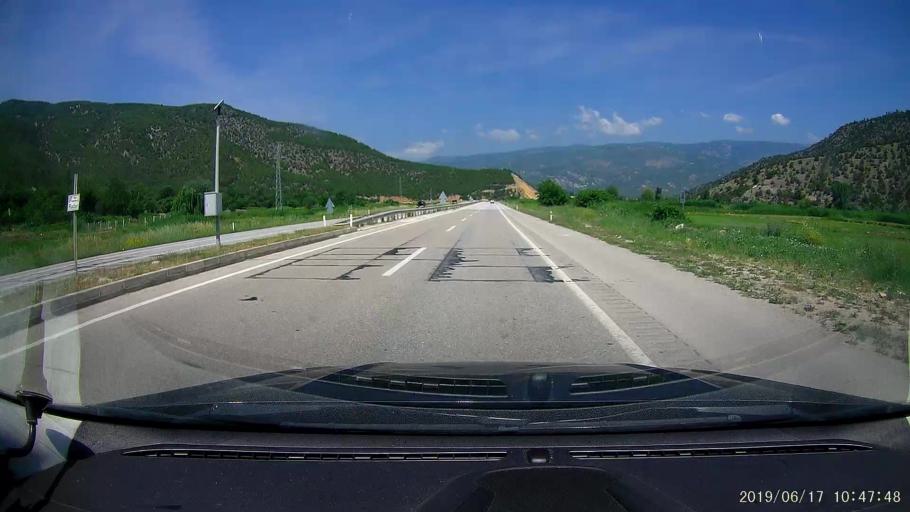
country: TR
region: Corum
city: Hacihamza
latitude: 41.0807
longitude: 34.4422
